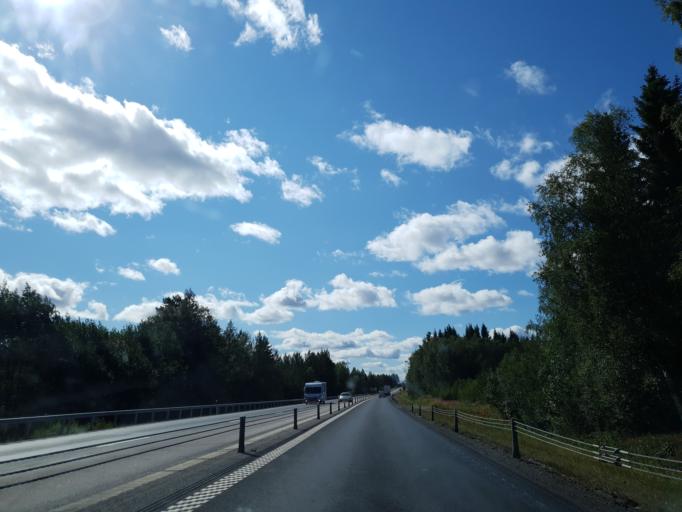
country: SE
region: Vaesterbotten
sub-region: Nordmalings Kommun
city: Nordmaling
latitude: 63.5243
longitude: 19.3846
